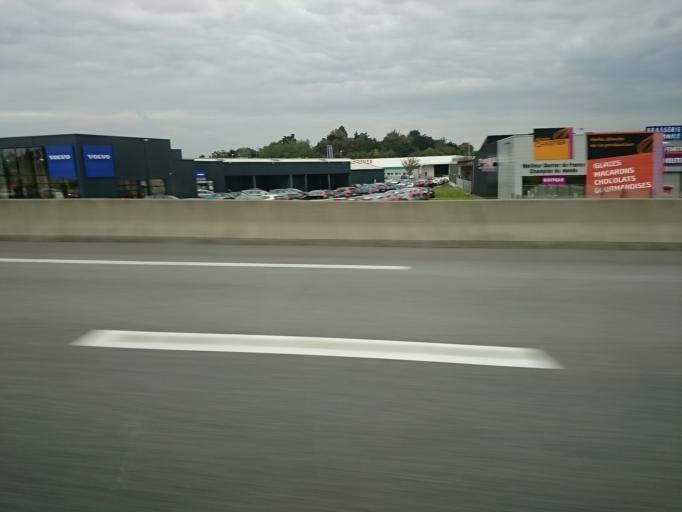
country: FR
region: Brittany
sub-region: Departement du Morbihan
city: Sene
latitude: 47.6454
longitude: -2.6991
